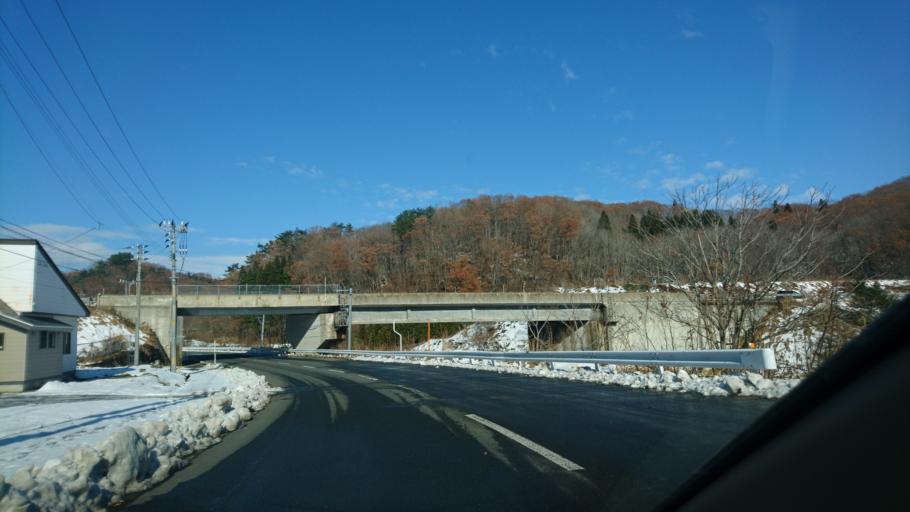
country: JP
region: Akita
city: Yokotemachi
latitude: 39.3156
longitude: 140.7562
